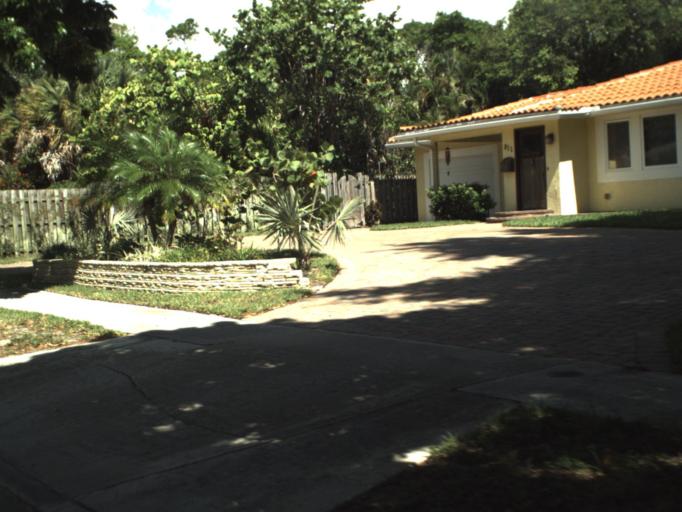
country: US
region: Florida
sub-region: Palm Beach County
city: Lake Clarke Shores
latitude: 26.6553
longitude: -80.0624
